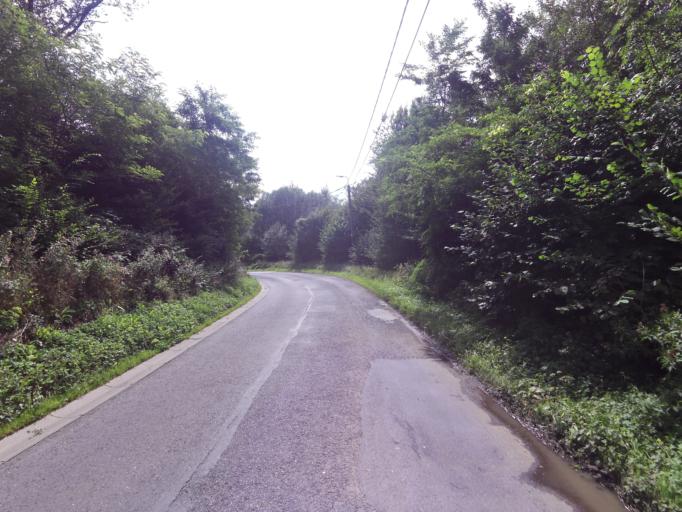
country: BE
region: Wallonia
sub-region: Province de Liege
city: Amay
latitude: 50.5632
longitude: 5.3326
